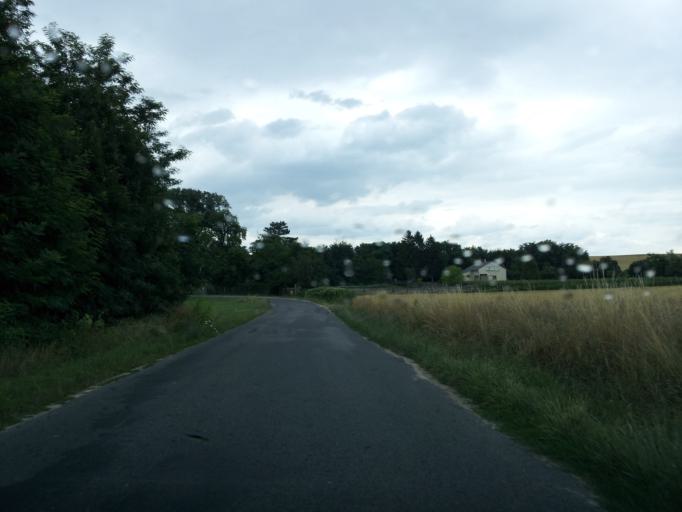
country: HU
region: Vas
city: Janoshaza
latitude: 47.0896
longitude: 17.0498
